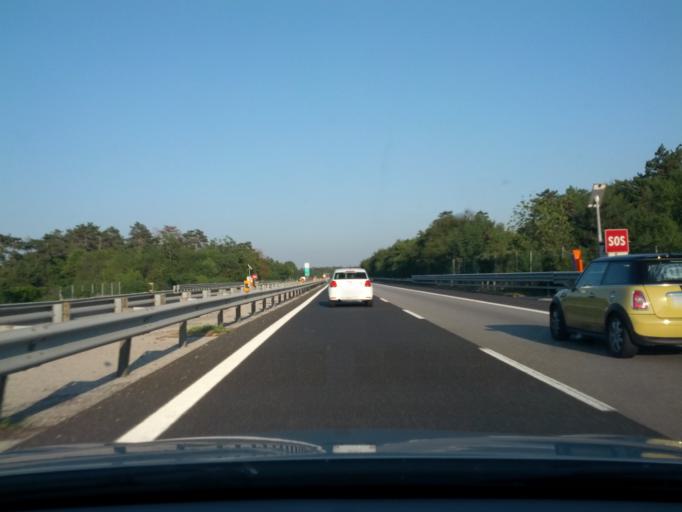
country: IT
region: Friuli Venezia Giulia
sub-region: Provincia di Trieste
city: Prosecco-Contovello
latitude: 45.7019
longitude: 13.7568
